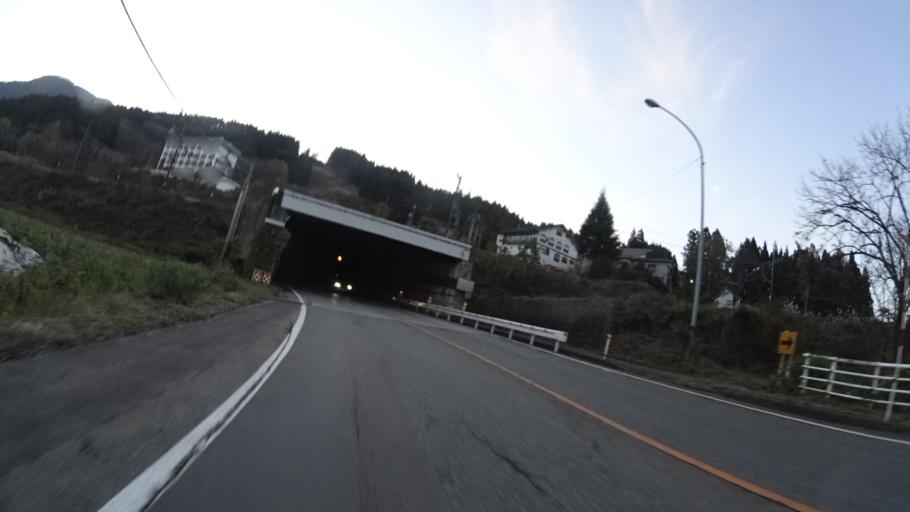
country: JP
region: Niigata
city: Shiozawa
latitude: 36.9754
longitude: 138.8018
